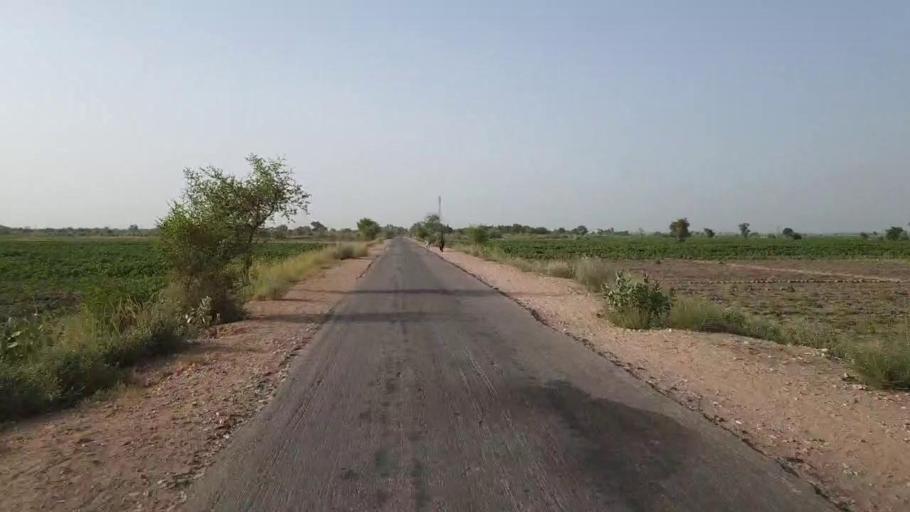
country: PK
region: Sindh
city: Jam Sahib
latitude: 26.4752
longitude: 68.8598
